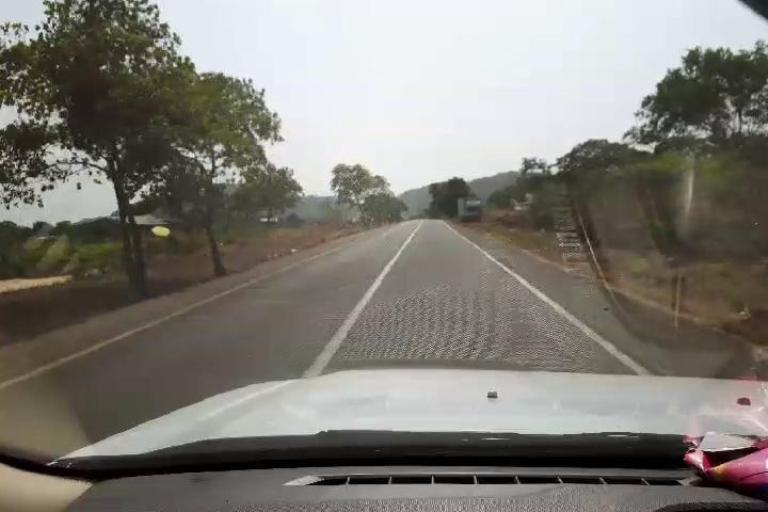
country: SL
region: Western Area
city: Waterloo
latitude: 8.2027
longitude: -13.1274
